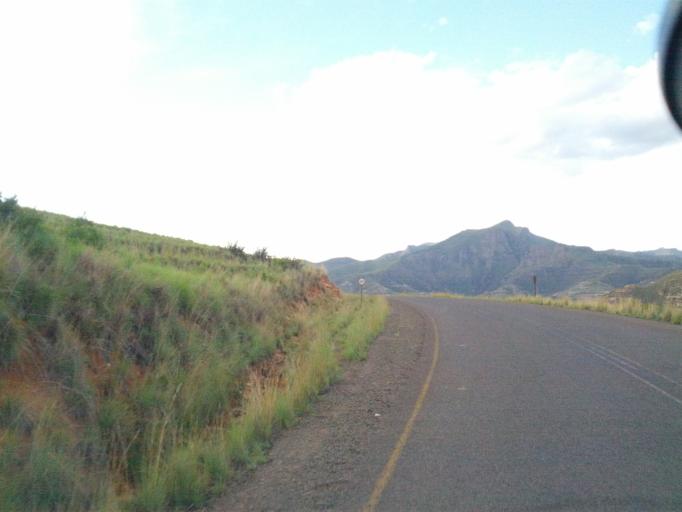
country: LS
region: Qacha's Nek
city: Qacha's Nek
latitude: -30.0754
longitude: 28.5796
